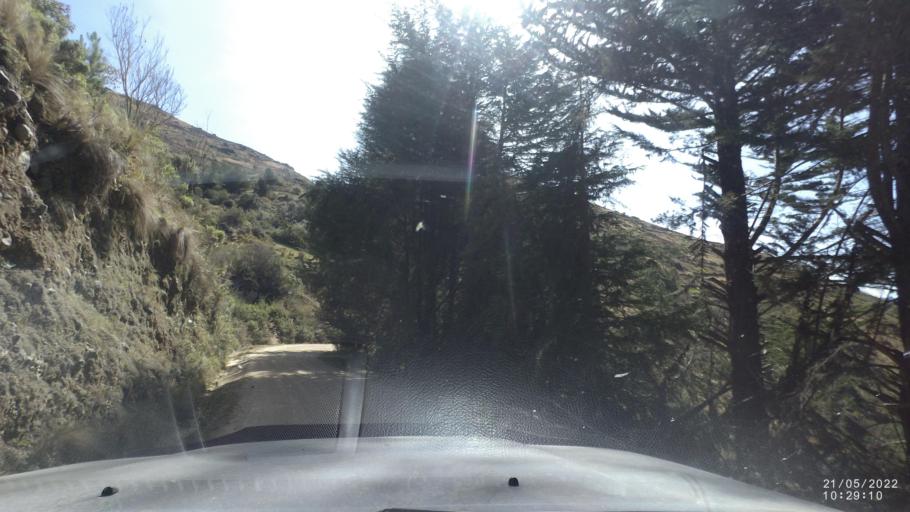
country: BO
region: Cochabamba
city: Colomi
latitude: -17.3206
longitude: -65.9393
